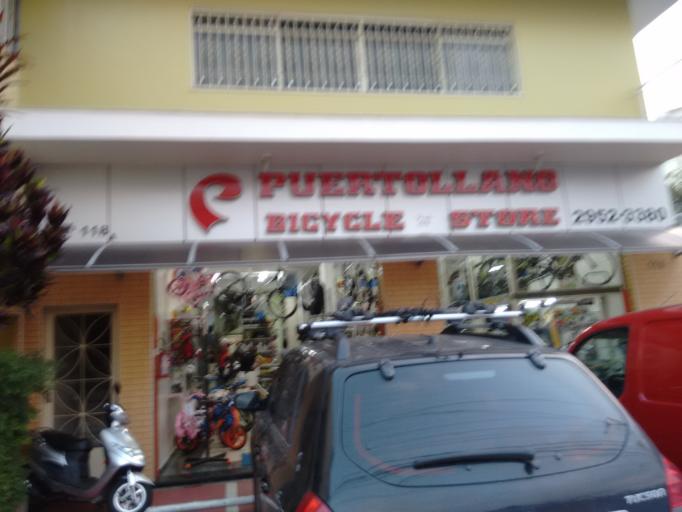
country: BR
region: Sao Paulo
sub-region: Sao Paulo
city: Sao Paulo
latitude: -23.4606
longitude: -46.6228
